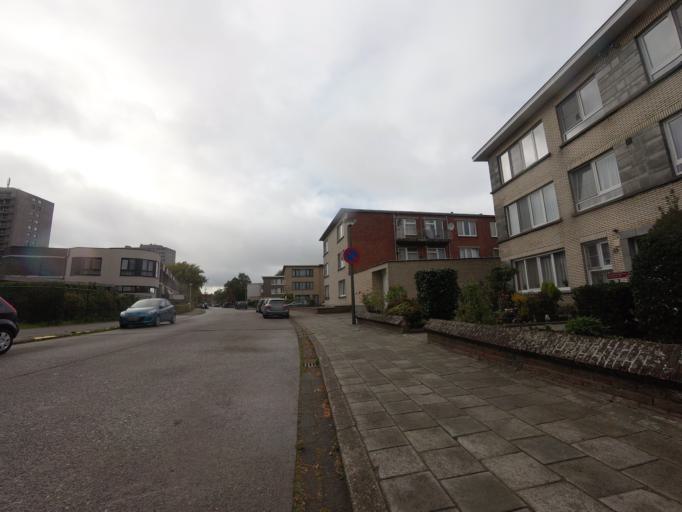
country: BE
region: Flanders
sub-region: Provincie Antwerpen
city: Borsbeek
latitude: 51.2308
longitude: 4.4652
